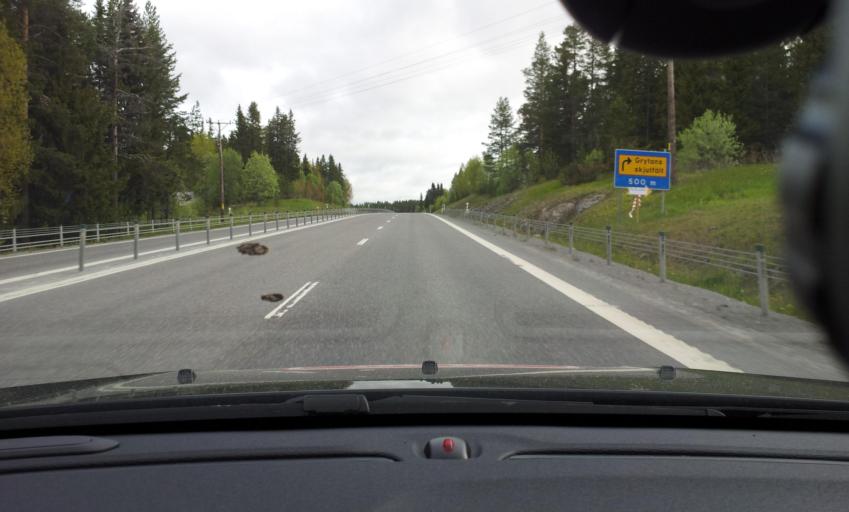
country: SE
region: Jaemtland
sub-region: OEstersunds Kommun
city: Brunflo
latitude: 63.1131
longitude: 14.7974
